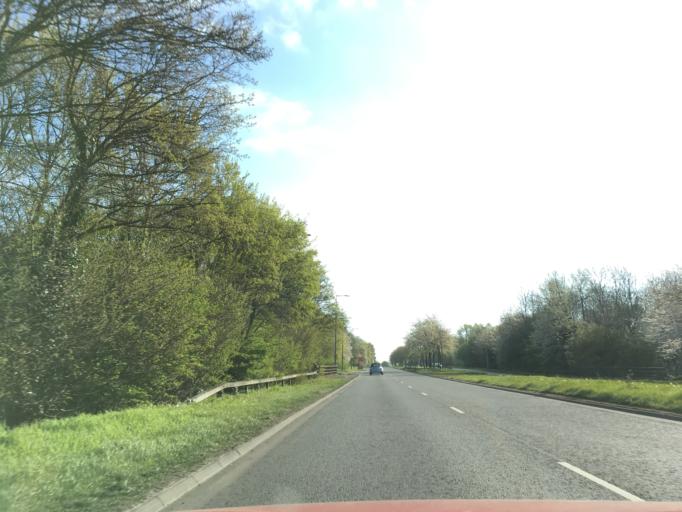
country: GB
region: England
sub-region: Milton Keynes
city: Bradwell
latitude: 52.0550
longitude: -0.7818
